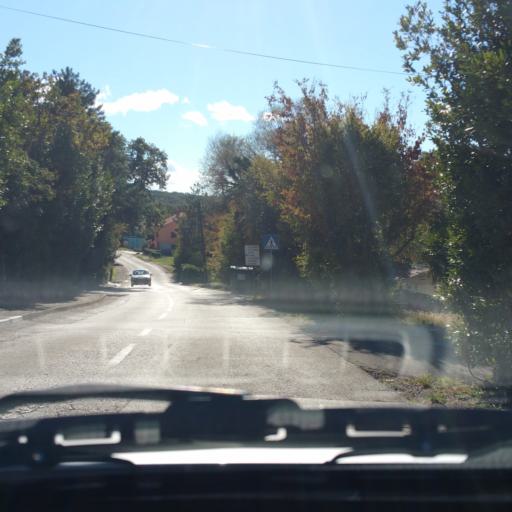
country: HR
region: Primorsko-Goranska
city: Njivice
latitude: 45.1592
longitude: 14.5376
